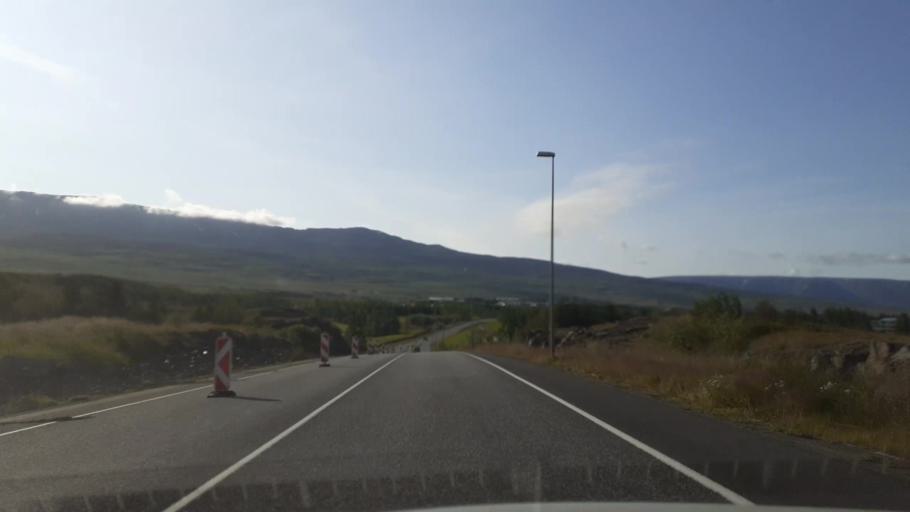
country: IS
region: Northeast
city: Akureyri
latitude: 65.6710
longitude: -18.1142
